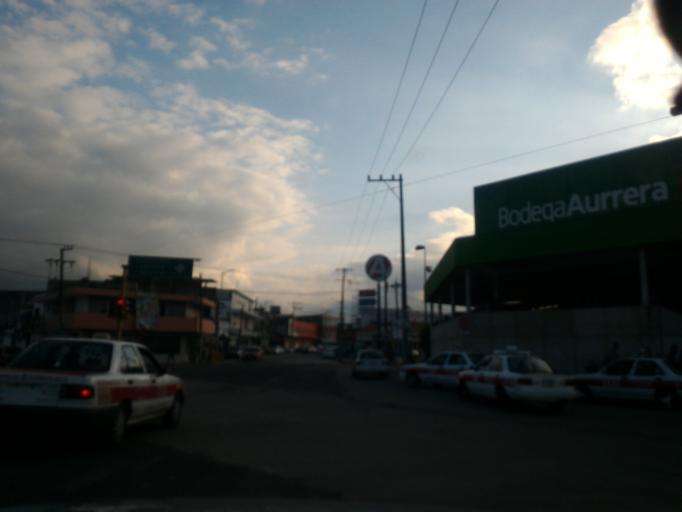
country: MX
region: Veracruz
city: Martinez de la Torre
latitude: 20.0664
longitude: -97.0493
